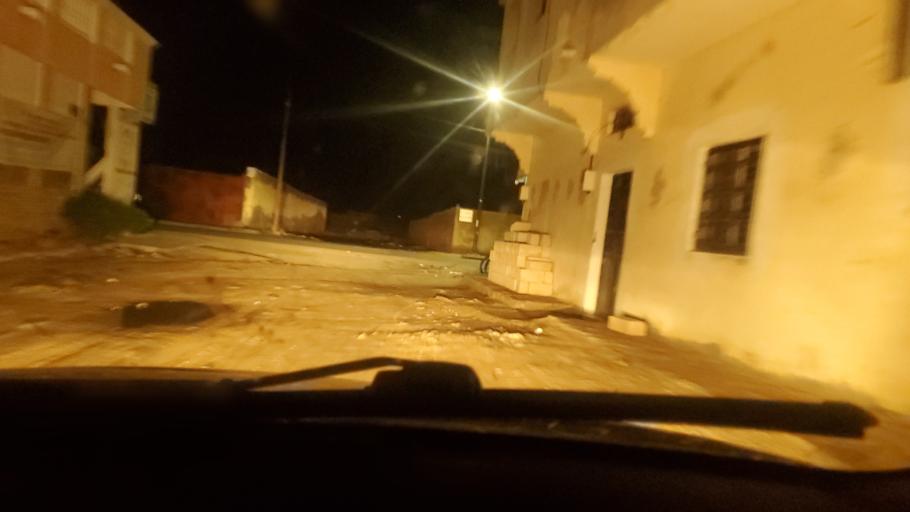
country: SN
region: Saint-Louis
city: Saint-Louis
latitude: 16.0263
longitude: -16.4798
